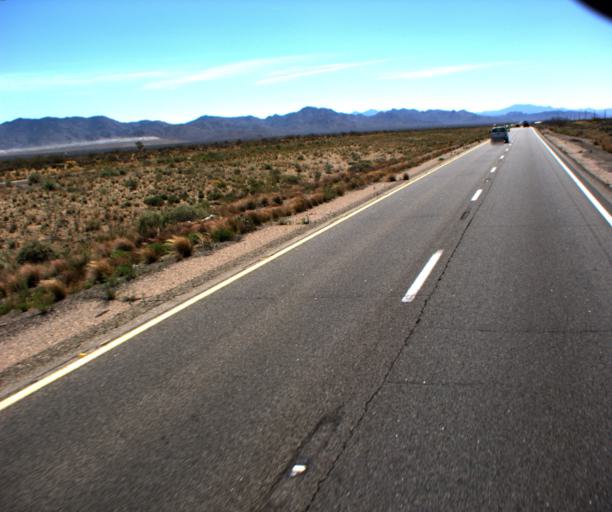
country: US
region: Arizona
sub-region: Mohave County
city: Golden Valley
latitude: 35.3595
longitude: -114.2326
